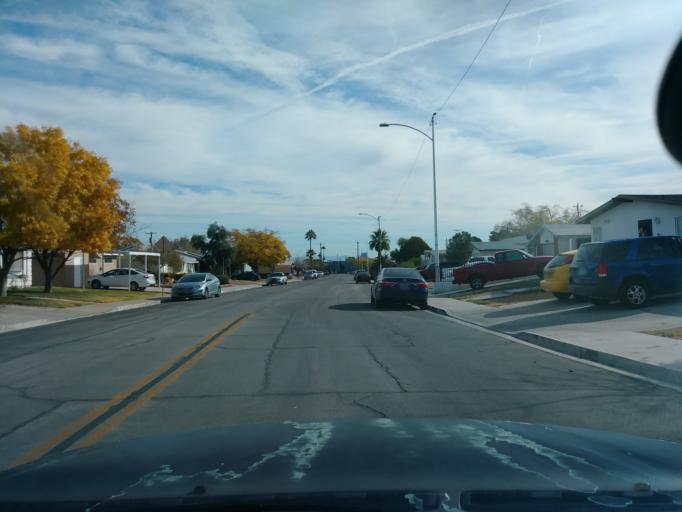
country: US
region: Nevada
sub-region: Clark County
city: Spring Valley
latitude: 36.1614
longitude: -115.2396
